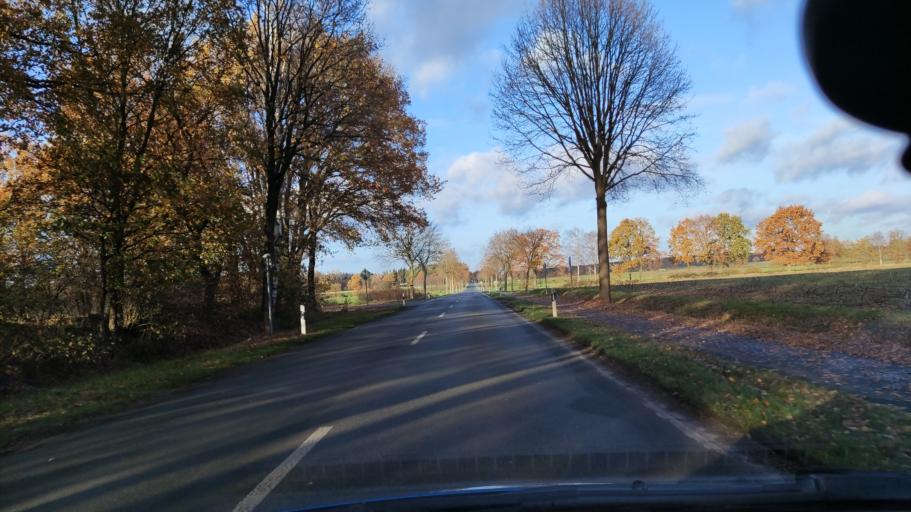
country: DE
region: Lower Saxony
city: Soltau
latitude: 53.0359
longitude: 9.8288
